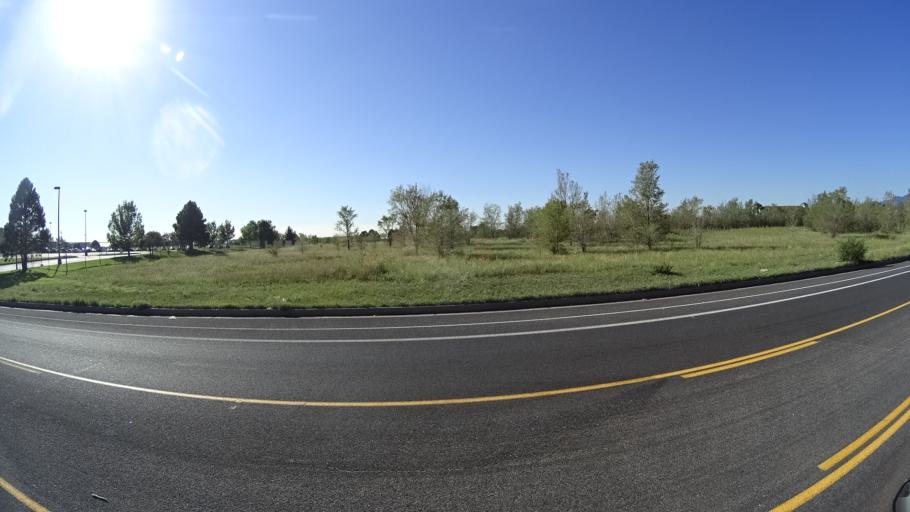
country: US
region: Colorado
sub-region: El Paso County
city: Stratmoor
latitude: 38.8087
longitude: -104.7347
